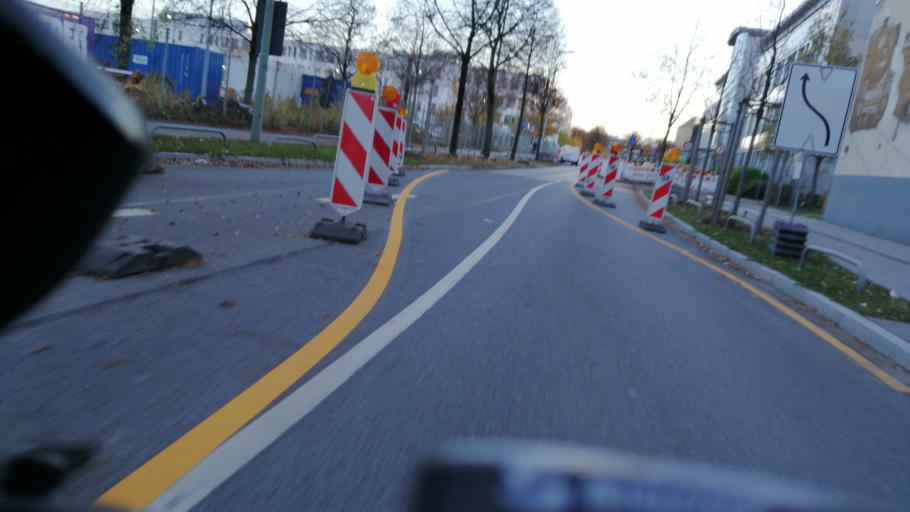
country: DE
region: Bavaria
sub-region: Upper Bavaria
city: Unterfoehring
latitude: 48.1946
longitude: 11.6086
